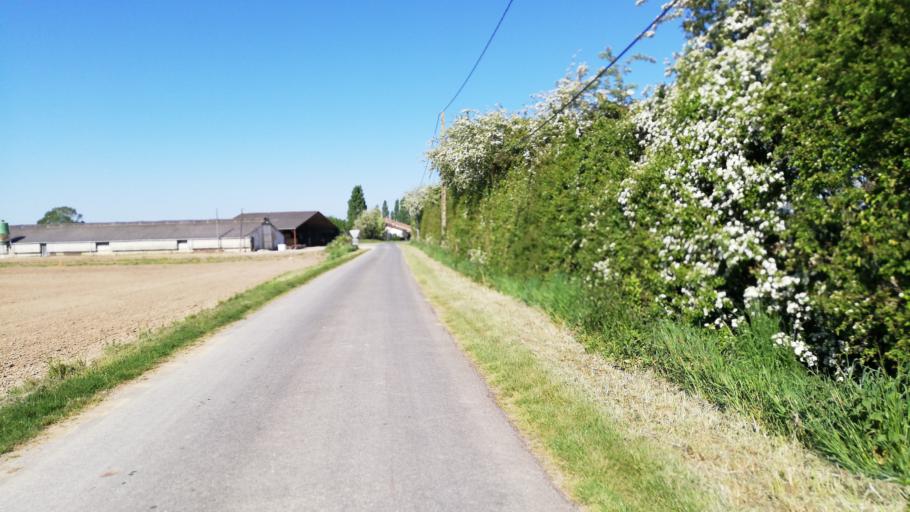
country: FR
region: Pays de la Loire
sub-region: Departement de la Vendee
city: Maillezais
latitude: 46.3261
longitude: -0.7430
